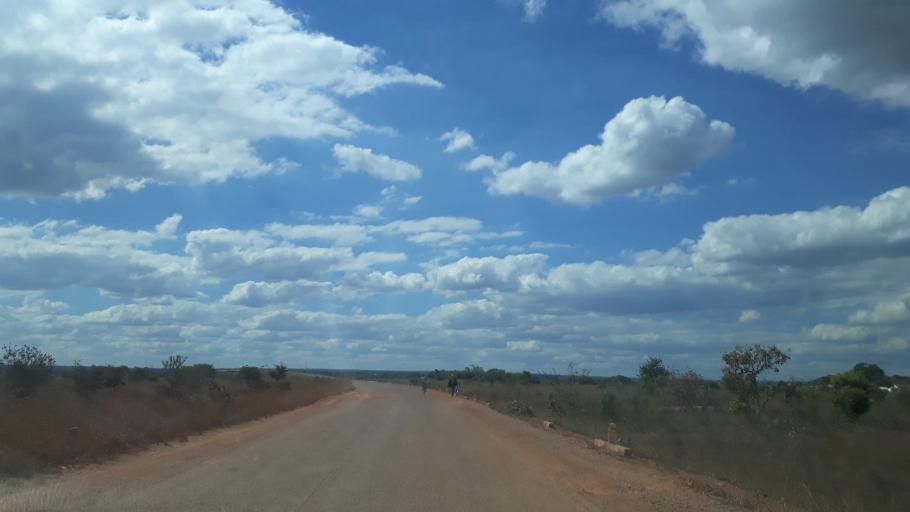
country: ZM
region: Copperbelt
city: Mufulira
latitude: -11.9908
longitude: 28.7298
